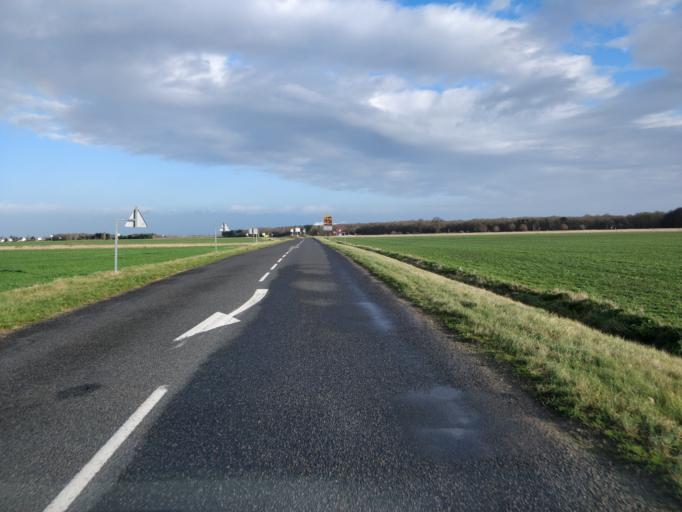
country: FR
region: Centre
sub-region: Departement du Loir-et-Cher
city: Muides-sur-Loire
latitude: 47.6589
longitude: 1.5347
